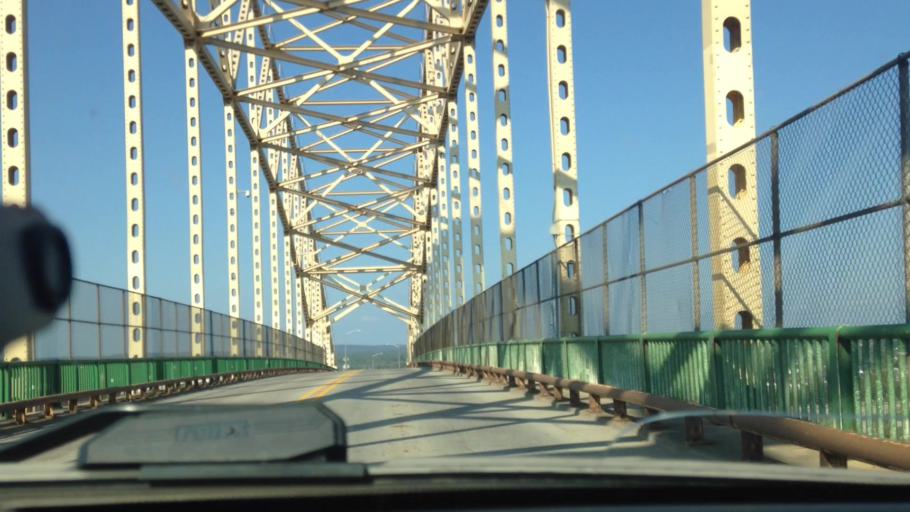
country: US
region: Michigan
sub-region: Chippewa County
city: Sault Ste. Marie
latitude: 46.5125
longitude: -84.3591
